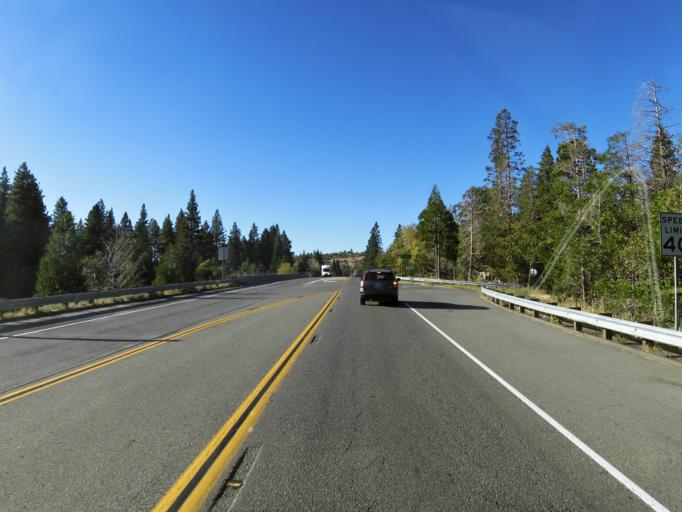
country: US
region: California
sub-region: Siskiyou County
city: Weed
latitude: 41.4235
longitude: -122.3875
